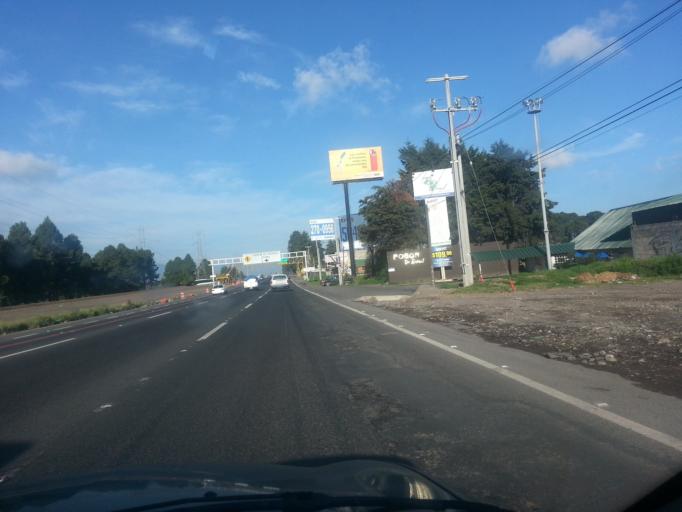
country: MX
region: Morelos
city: Ocoyoacac
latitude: 19.2872
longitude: -99.4468
